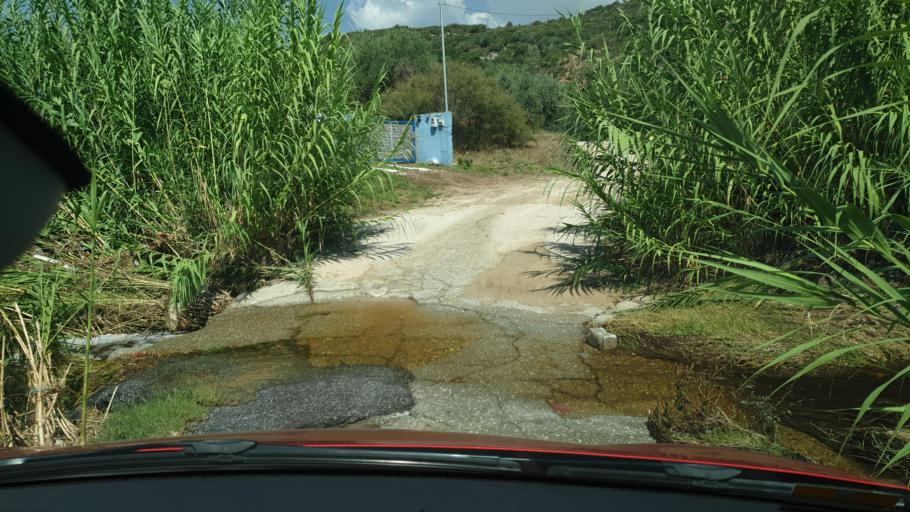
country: GR
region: Central Macedonia
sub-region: Nomos Chalkidikis
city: Sykia
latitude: 39.9858
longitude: 23.9076
